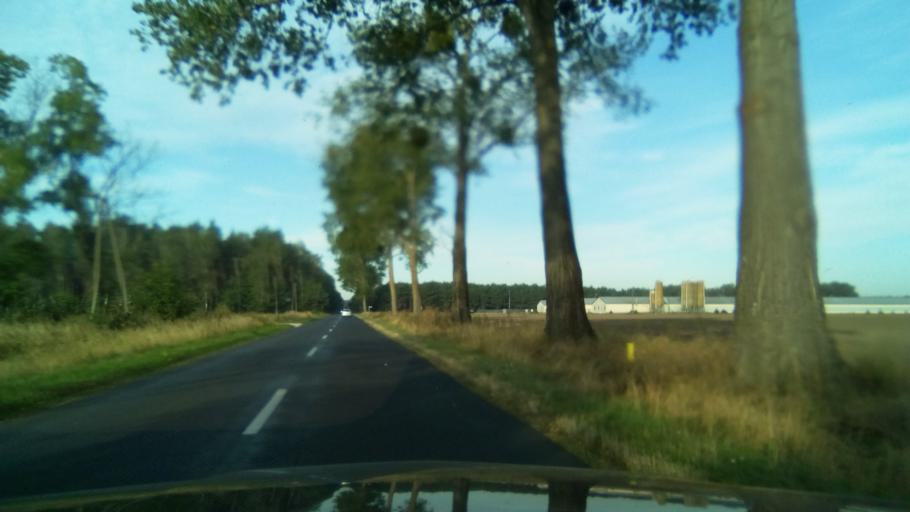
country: PL
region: Greater Poland Voivodeship
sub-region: Powiat chodzieski
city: Budzyn
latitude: 52.8756
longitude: 17.0807
